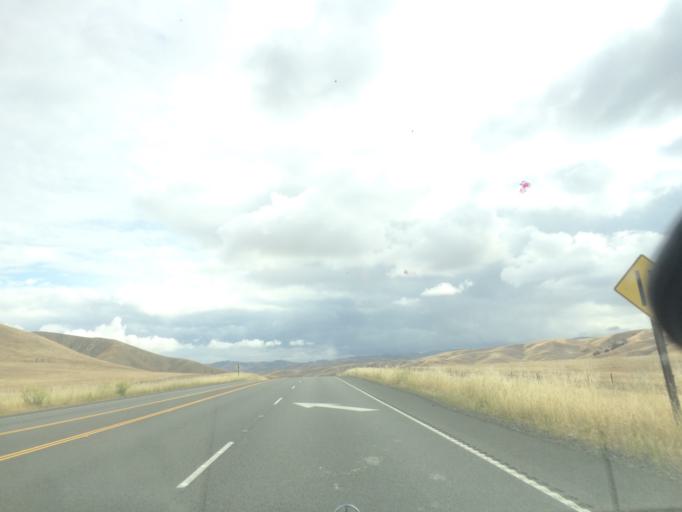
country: US
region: California
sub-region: San Luis Obispo County
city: Shandon
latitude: 35.7117
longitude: -120.3091
